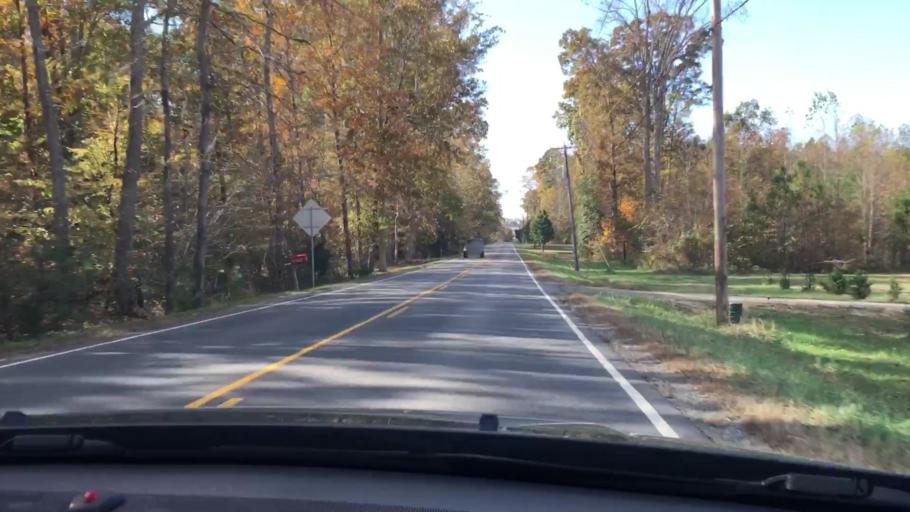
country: US
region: Virginia
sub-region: King and Queen County
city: King and Queen Court House
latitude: 37.5911
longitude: -76.8739
